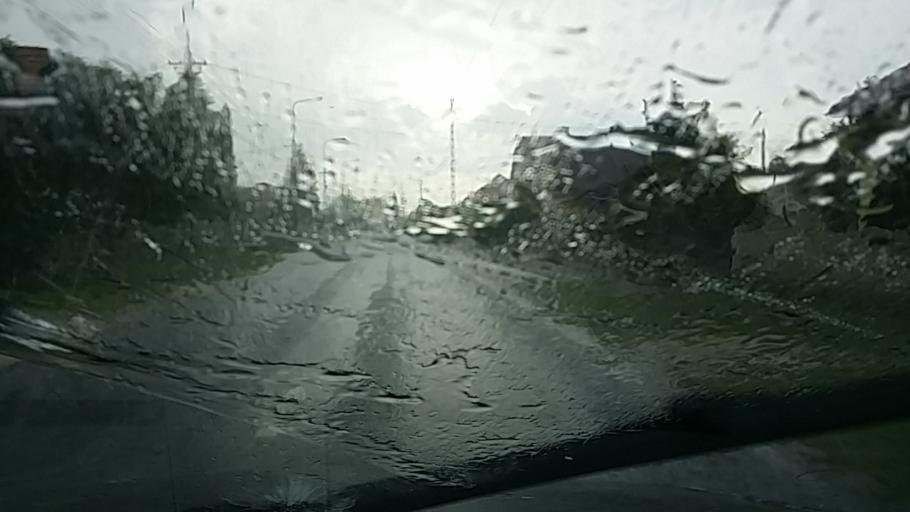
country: HU
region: Pest
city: Ocsa
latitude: 47.2923
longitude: 19.2355
